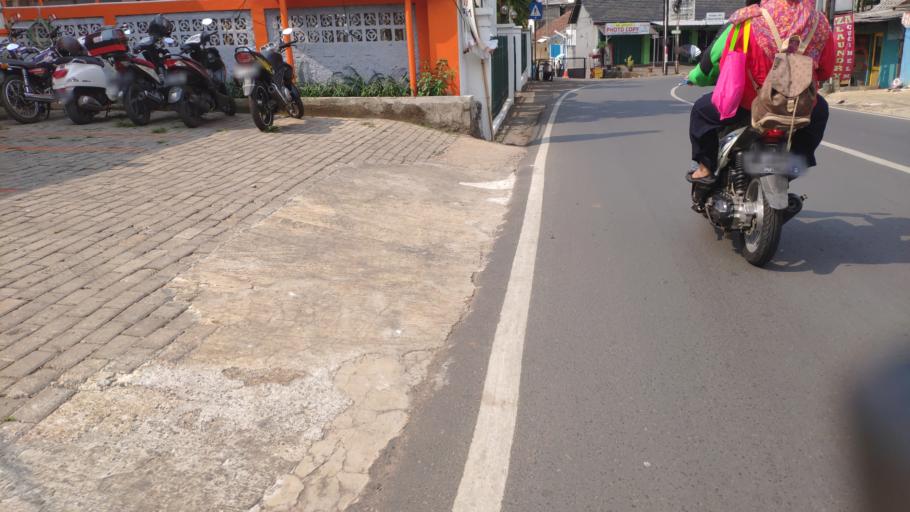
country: ID
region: West Java
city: Pamulang
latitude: -6.3182
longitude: 106.8112
